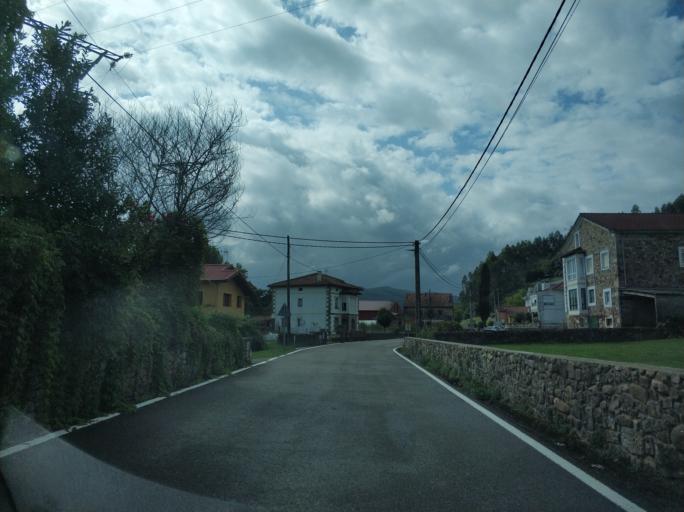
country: ES
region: Cantabria
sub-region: Provincia de Cantabria
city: Polanco
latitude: 43.3689
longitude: -3.9688
